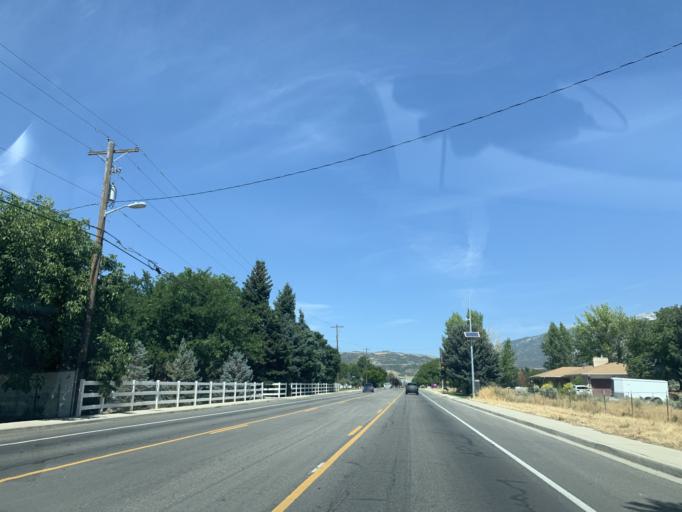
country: US
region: Utah
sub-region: Utah County
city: Lehi
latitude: 40.4098
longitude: -111.8302
